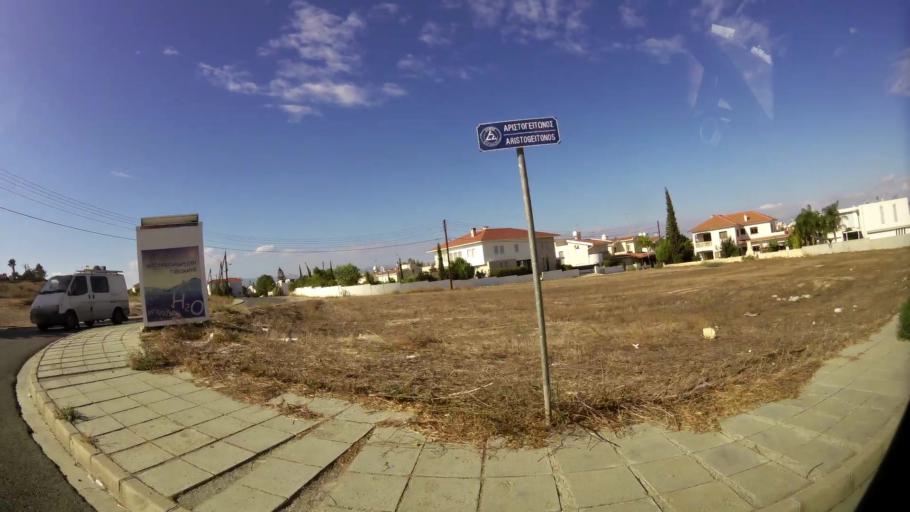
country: CY
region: Lefkosia
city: Nicosia
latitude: 35.1264
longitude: 33.3431
